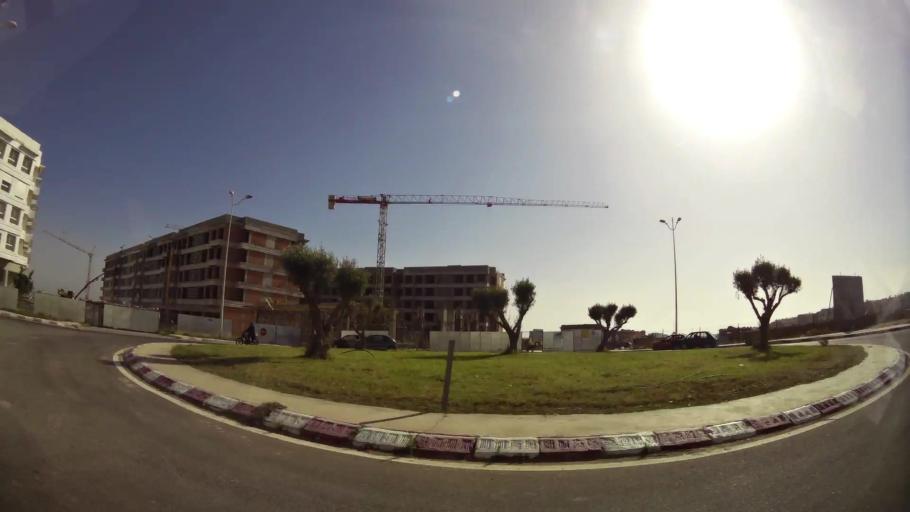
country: MA
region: Oued ed Dahab-Lagouira
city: Dakhla
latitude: 30.4084
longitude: -9.5666
